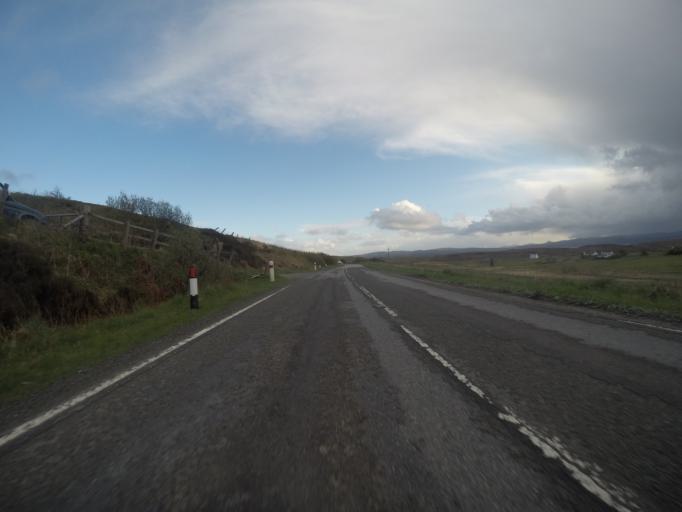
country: GB
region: Scotland
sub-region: Highland
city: Portree
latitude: 57.5641
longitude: -6.3644
